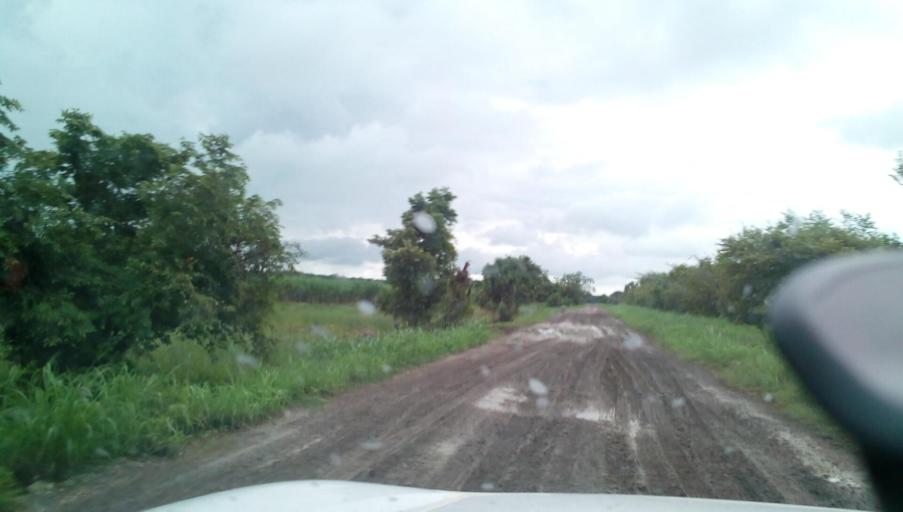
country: MX
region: Veracruz
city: Panuco
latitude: 21.8224
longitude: -98.1109
